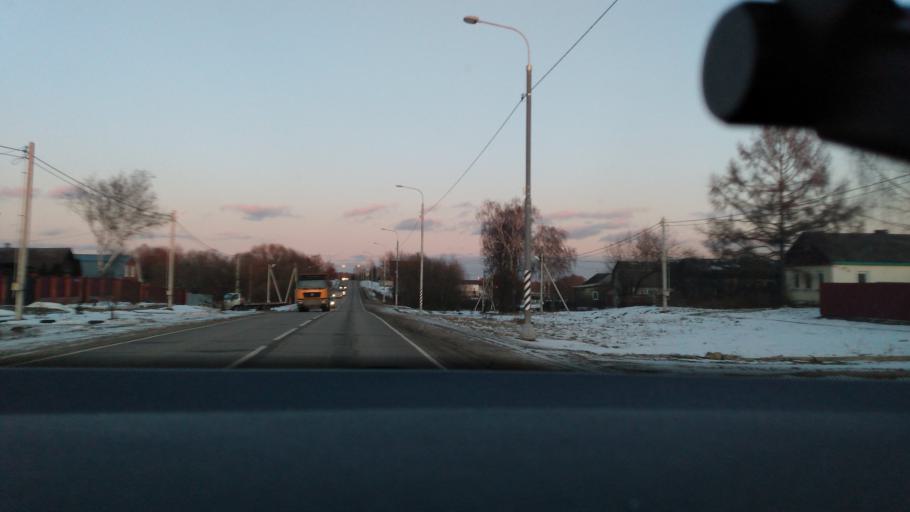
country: RU
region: Moskovskaya
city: Lukhovitsy
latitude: 55.0917
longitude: 38.9491
